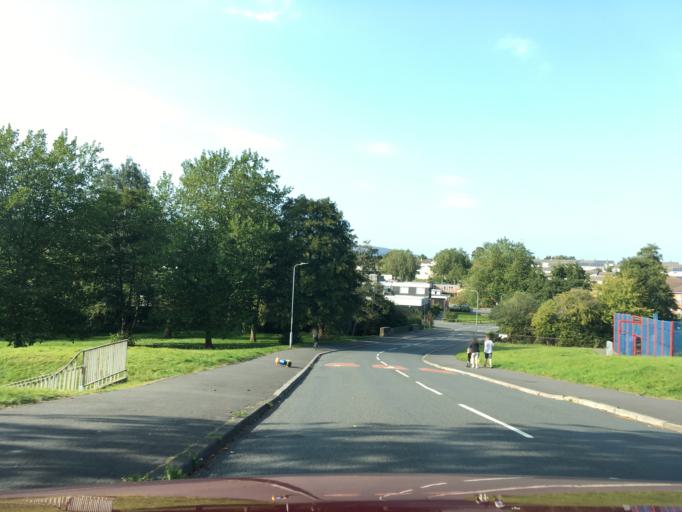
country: GB
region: Wales
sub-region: Newport
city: Newport
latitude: 51.6106
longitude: -3.0277
